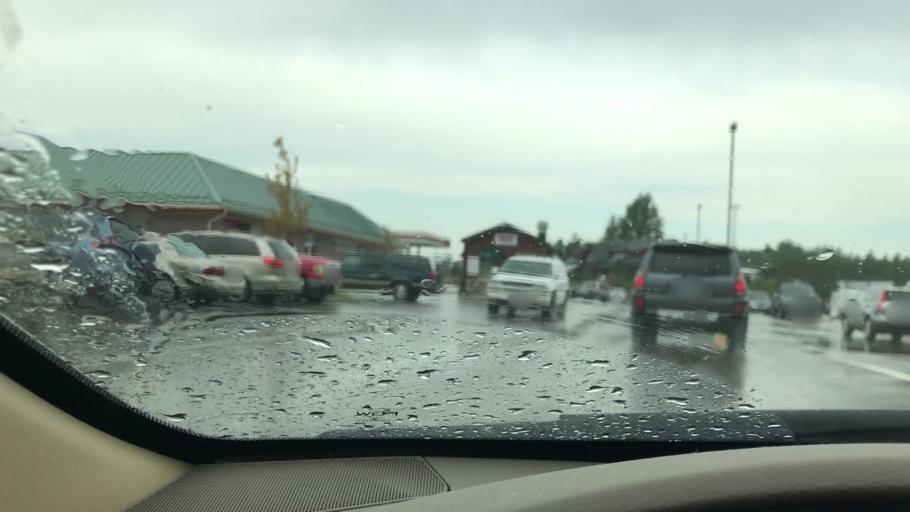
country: US
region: Minnesota
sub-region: Saint Louis County
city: Hermantown
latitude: 46.8229
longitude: -92.1858
